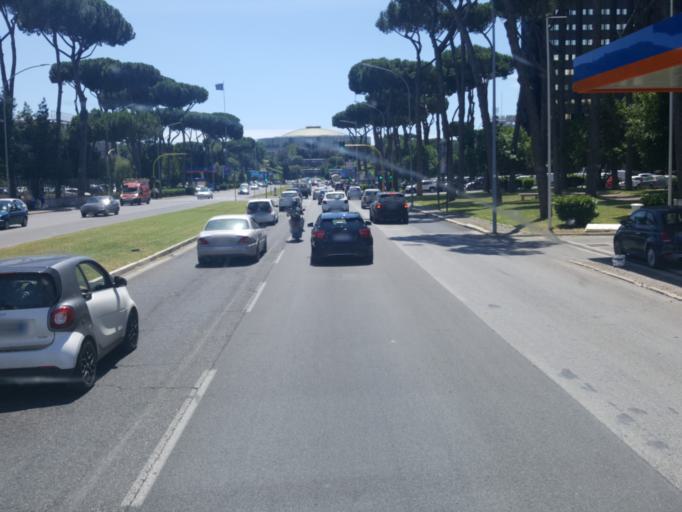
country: IT
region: Latium
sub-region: Citta metropolitana di Roma Capitale
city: Selcetta
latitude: 41.8318
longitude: 12.4697
